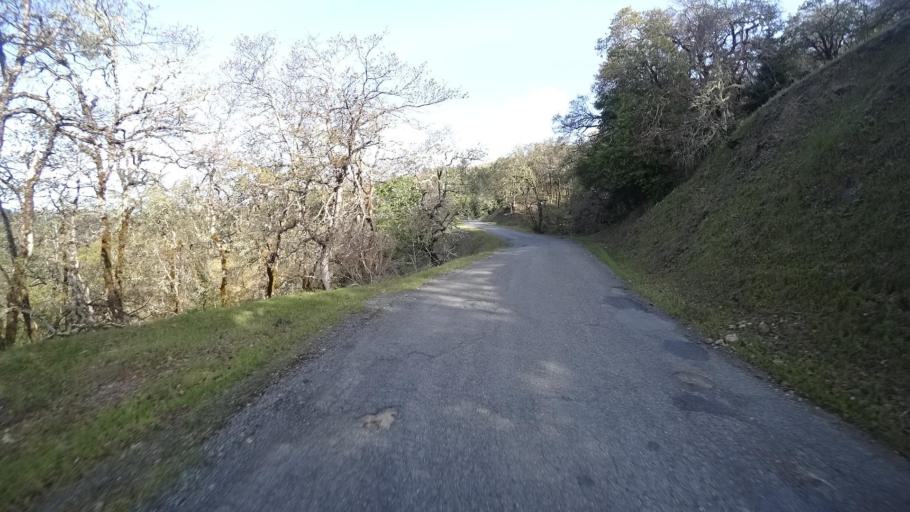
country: US
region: California
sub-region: Humboldt County
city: Hydesville
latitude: 40.6403
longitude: -123.9041
